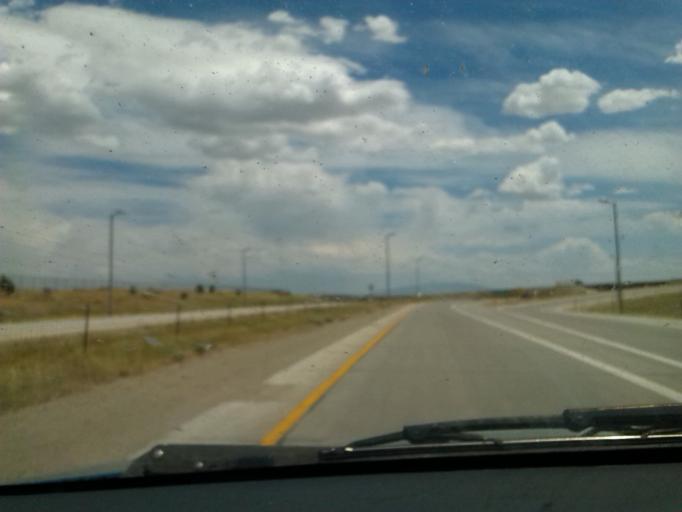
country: US
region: Wyoming
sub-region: Carbon County
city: Rawlins
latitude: 41.7910
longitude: -107.2044
